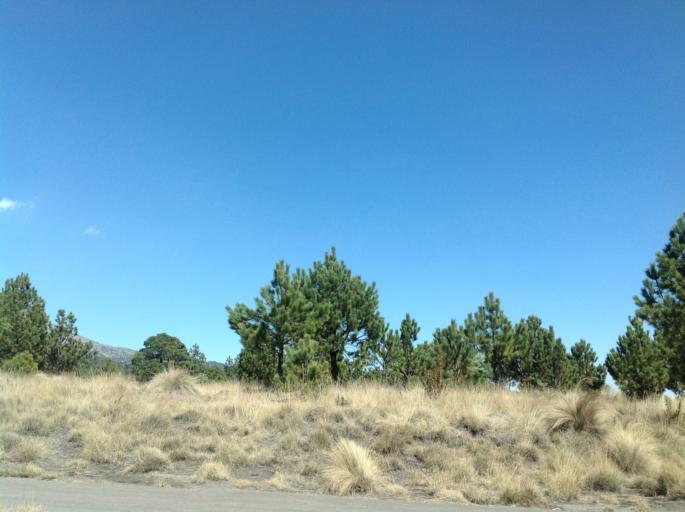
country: MX
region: Mexico
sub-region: Amecameca
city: San Diego Huehuecalco
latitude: 19.0931
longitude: -98.6495
